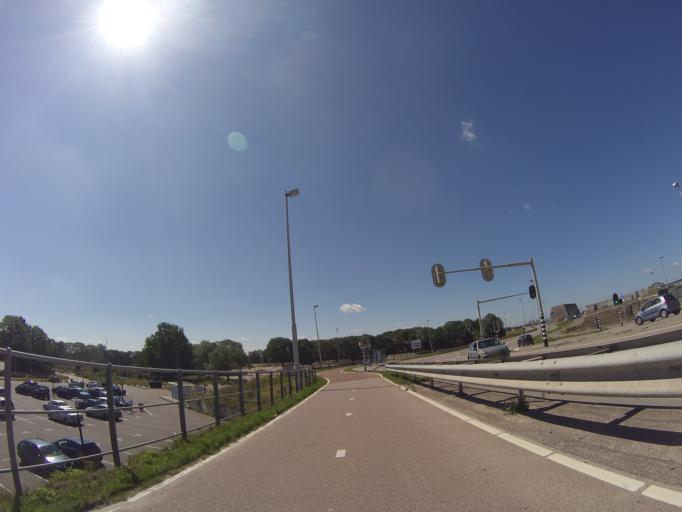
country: NL
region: Utrecht
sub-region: Gemeente Utrecht
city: Utrecht
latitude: 52.0965
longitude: 5.0740
